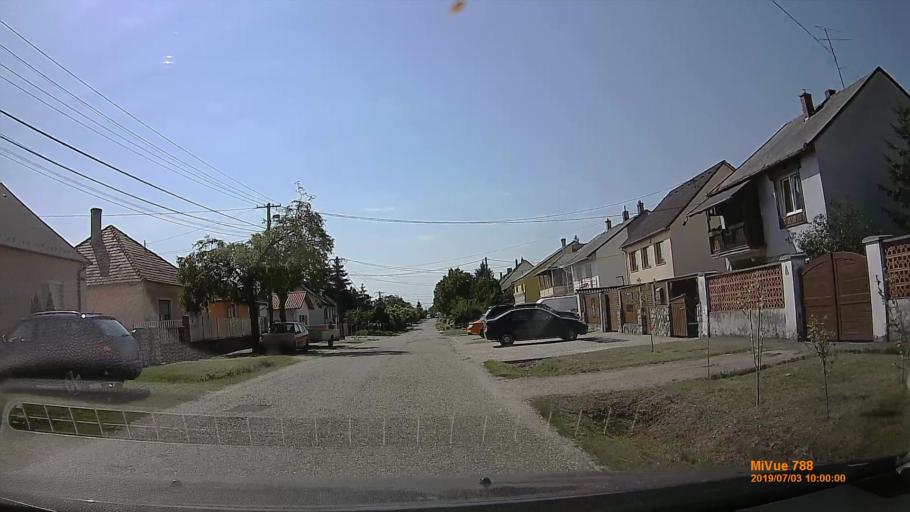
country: HU
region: Gyor-Moson-Sopron
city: Toltestava
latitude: 47.7097
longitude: 17.7237
